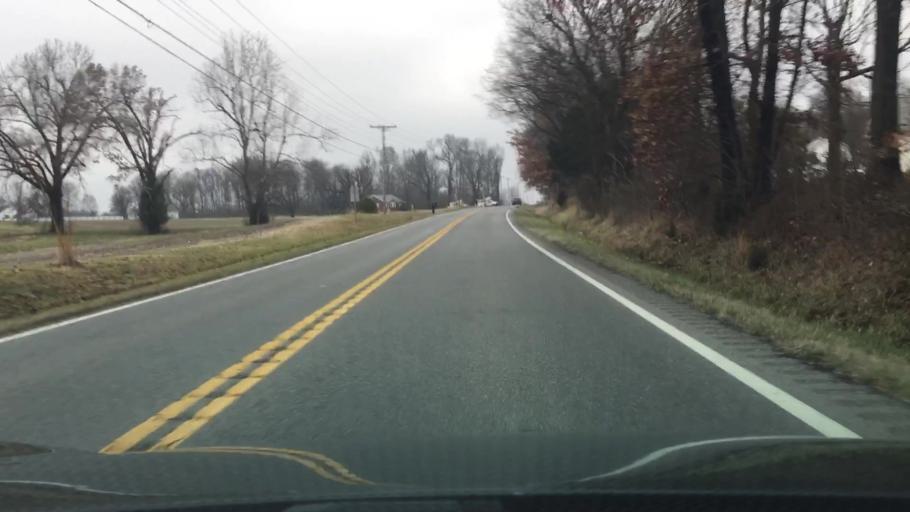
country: US
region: Kentucky
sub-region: Marshall County
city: Calvert City
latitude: 36.9487
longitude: -88.3672
